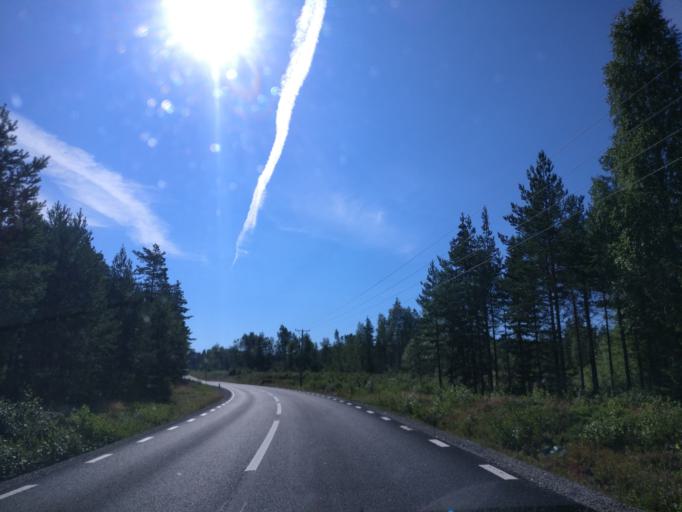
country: SE
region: Vaermland
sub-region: Hagfors Kommun
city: Hagfors
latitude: 60.0255
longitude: 13.8767
